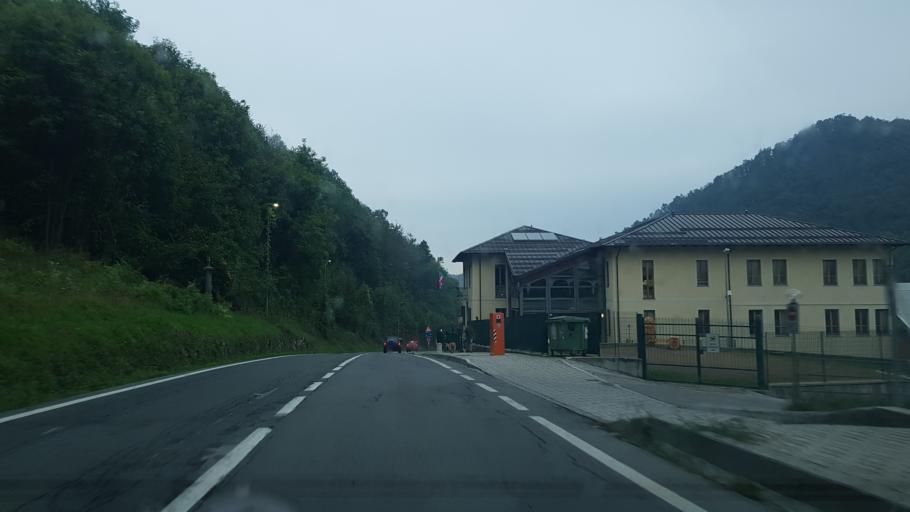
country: IT
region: Piedmont
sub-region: Provincia di Cuneo
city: Frabosa Sottana
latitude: 44.3052
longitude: 7.8007
